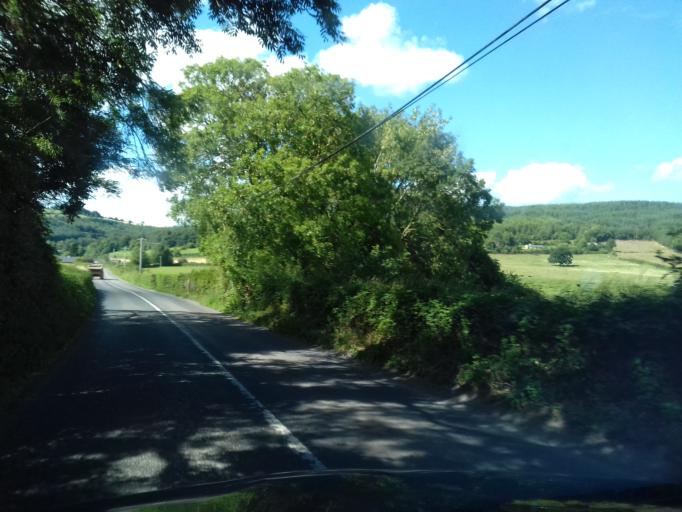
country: IE
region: Munster
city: Carrick-on-Suir
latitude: 52.3958
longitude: -7.4727
